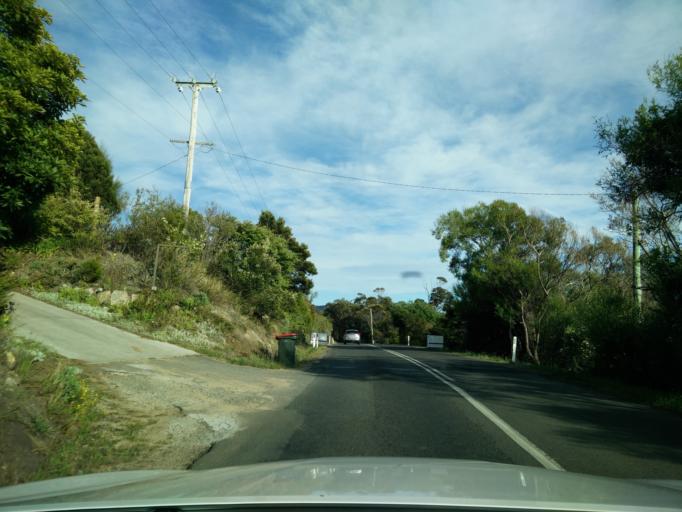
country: AU
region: Tasmania
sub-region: Break O'Day
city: St Helens
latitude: -41.8585
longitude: 148.2757
